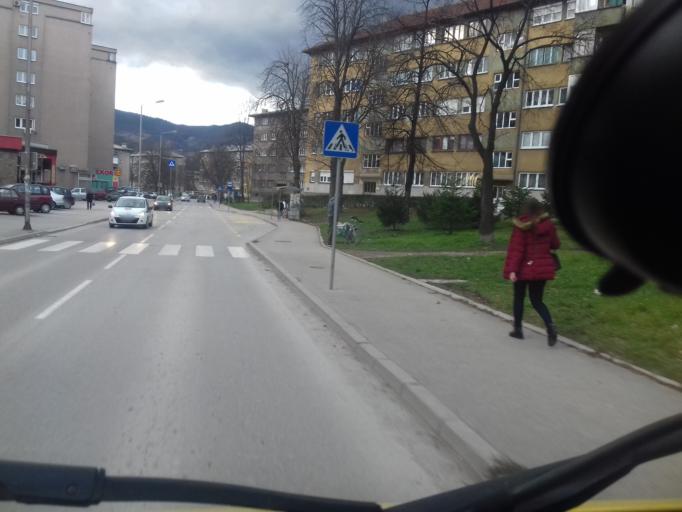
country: BA
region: Federation of Bosnia and Herzegovina
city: Zenica
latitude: 44.2035
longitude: 17.9221
